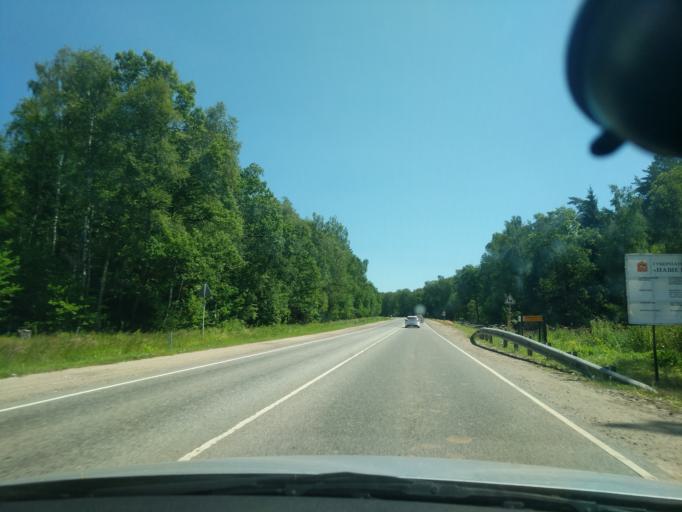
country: RU
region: Moskovskaya
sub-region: Chekhovskiy Rayon
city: Chekhov
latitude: 55.1437
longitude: 37.5073
